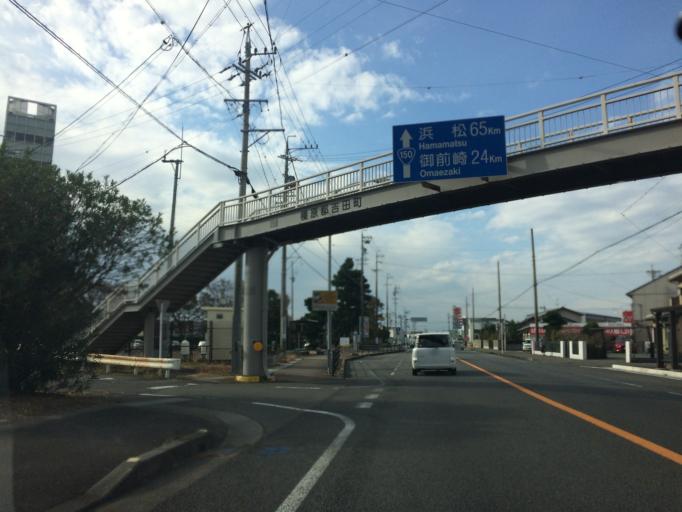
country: JP
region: Shizuoka
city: Shimada
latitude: 34.7719
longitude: 138.2516
